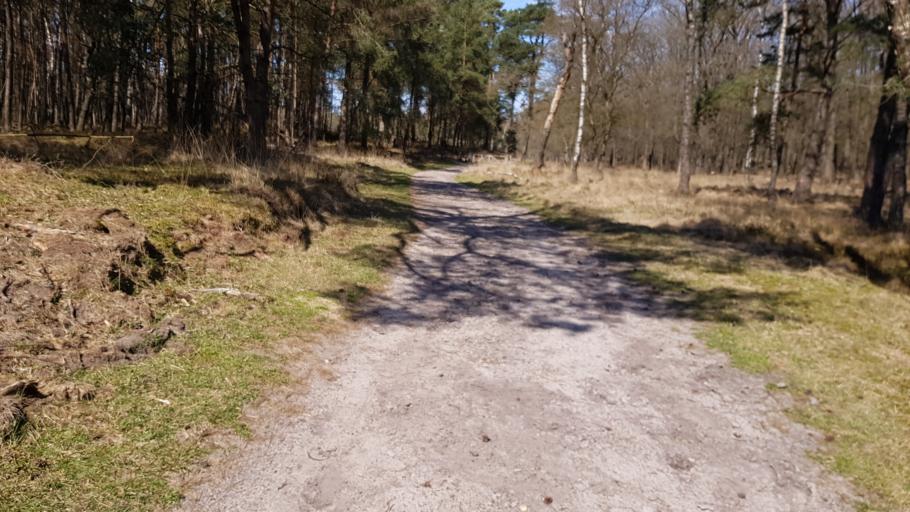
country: NL
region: Gelderland
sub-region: Gemeente Apeldoorn
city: Loenen
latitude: 52.0614
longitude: 6.0060
